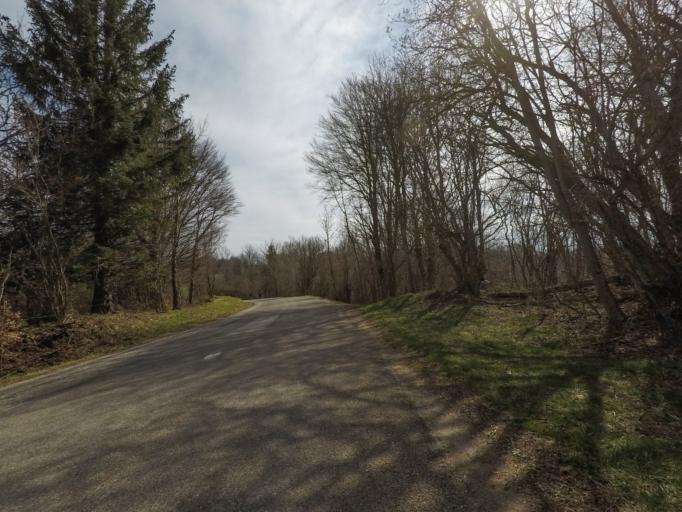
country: CH
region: Geneva
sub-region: Geneva
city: Veyrier
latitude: 46.1421
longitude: 6.1847
